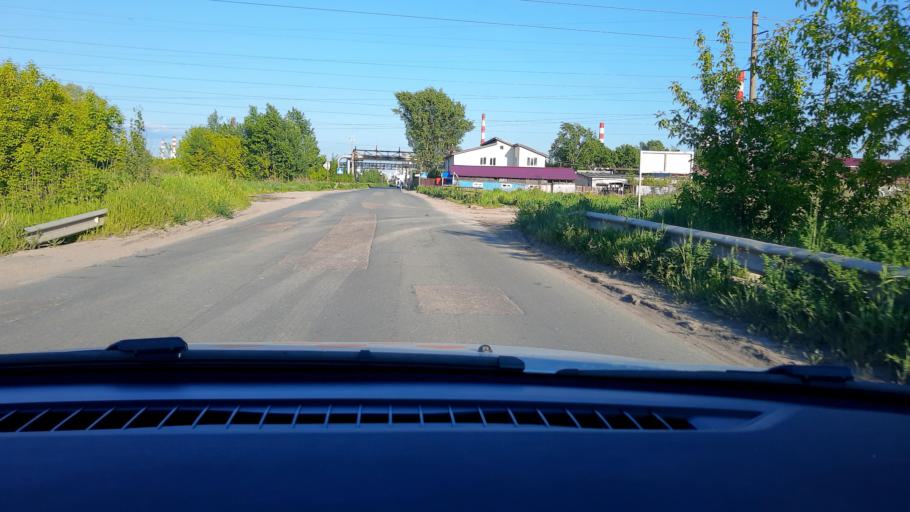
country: RU
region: Nizjnij Novgorod
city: Kstovo
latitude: 56.1030
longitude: 44.1348
